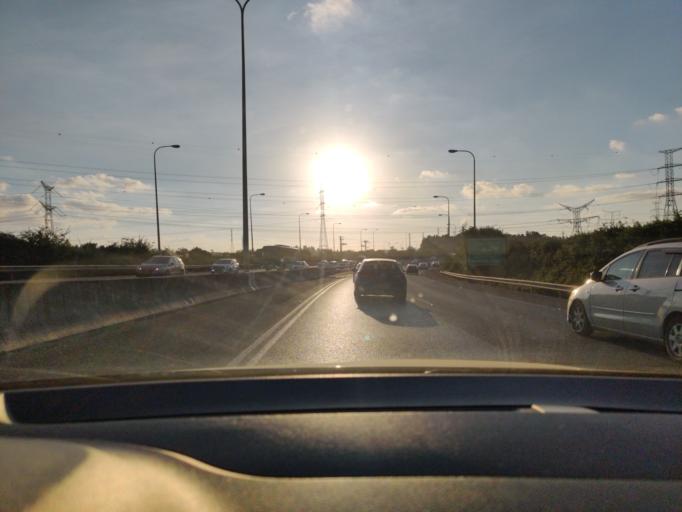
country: IL
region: Haifa
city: Hadera
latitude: 32.4462
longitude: 34.9464
